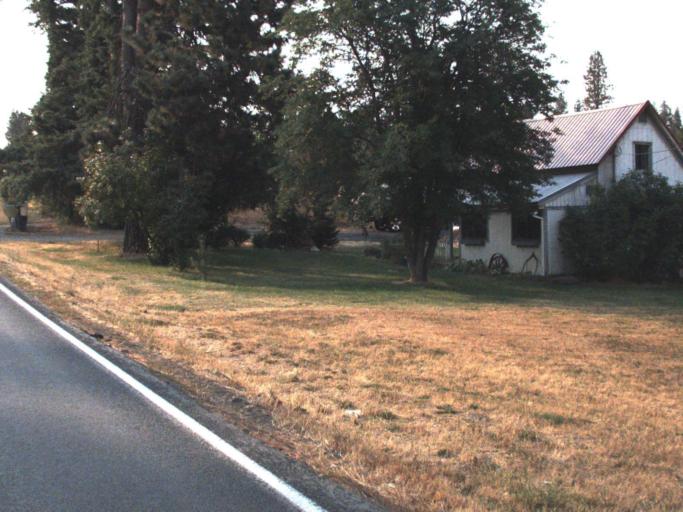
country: US
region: Washington
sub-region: Spokane County
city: Veradale
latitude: 47.4462
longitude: -117.1280
